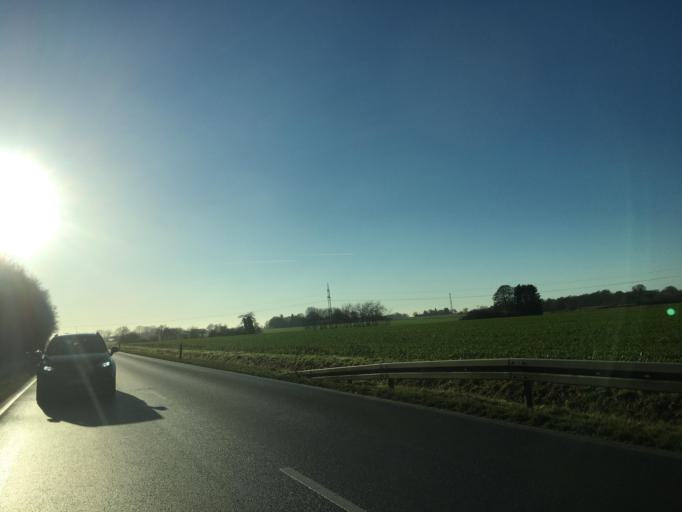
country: DE
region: North Rhine-Westphalia
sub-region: Regierungsbezirk Munster
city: Dulmen
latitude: 51.8736
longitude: 7.2880
